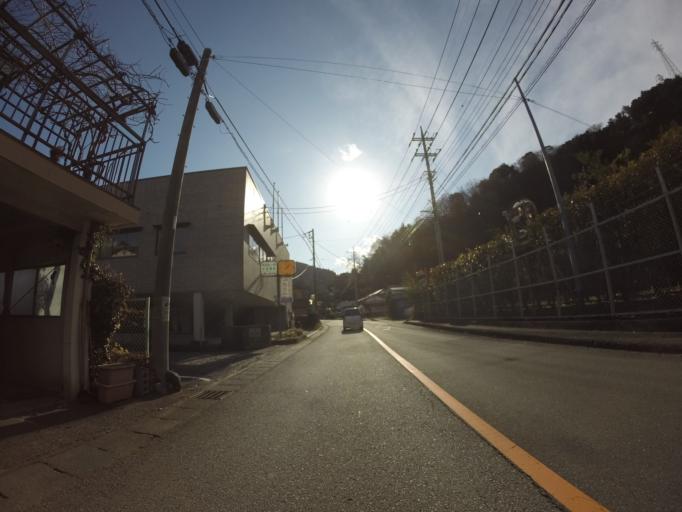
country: JP
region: Shizuoka
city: Fujinomiya
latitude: 35.3743
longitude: 138.4450
